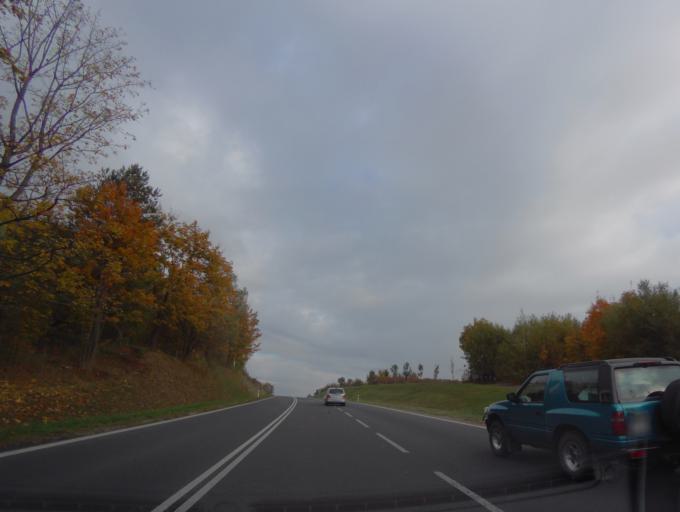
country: PL
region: Lublin Voivodeship
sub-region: Powiat bilgorajski
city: Frampol
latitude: 50.6815
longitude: 22.6785
